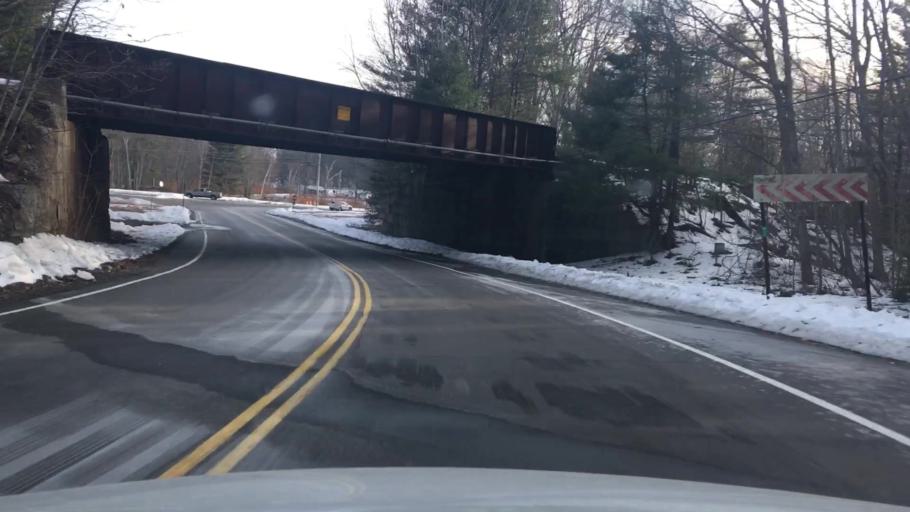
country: US
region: Maine
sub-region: York County
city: Wells Beach Station
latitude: 43.3459
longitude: -70.5616
